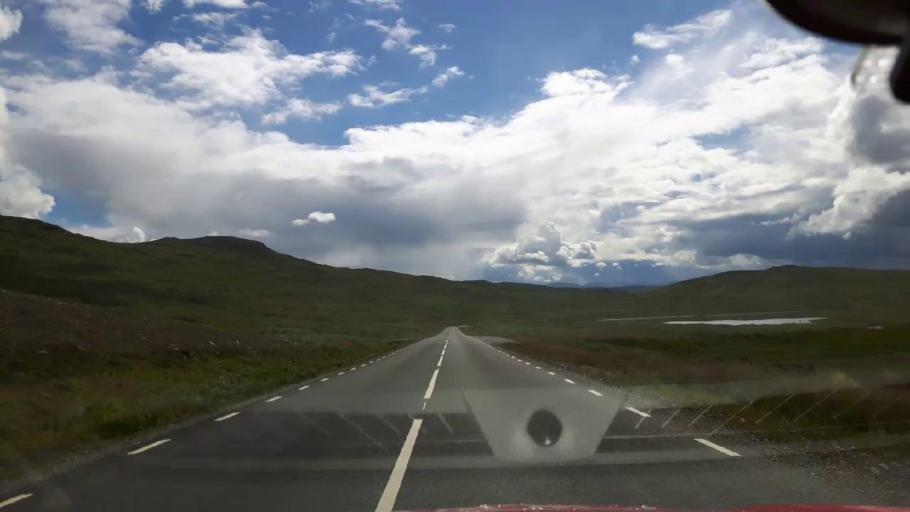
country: NO
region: Nordland
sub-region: Hattfjelldal
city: Hattfjelldal
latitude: 65.0357
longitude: 14.3300
